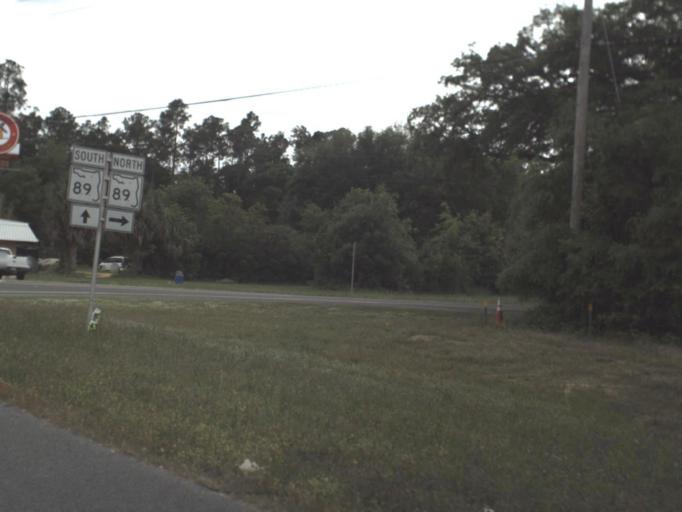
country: US
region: Florida
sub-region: Santa Rosa County
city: Point Baker
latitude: 30.6908
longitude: -87.0538
